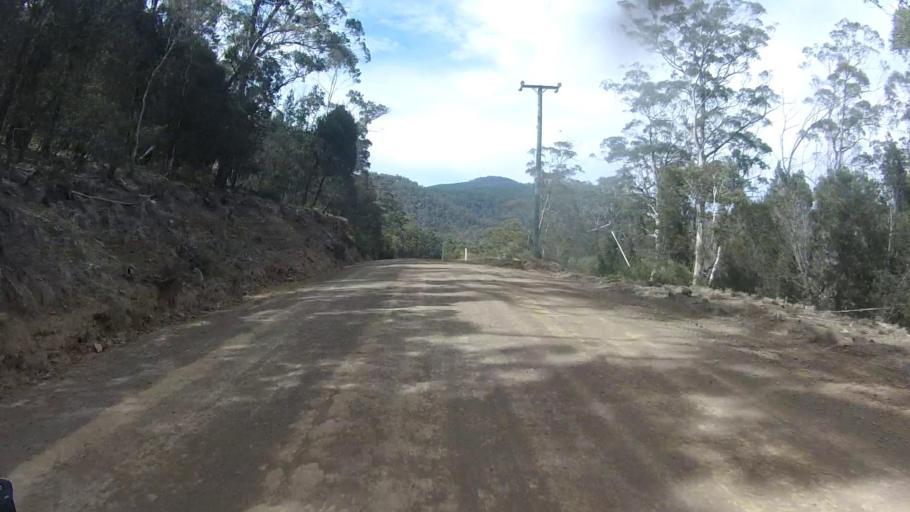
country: AU
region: Tasmania
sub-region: Sorell
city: Sorell
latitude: -42.6733
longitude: 147.8834
